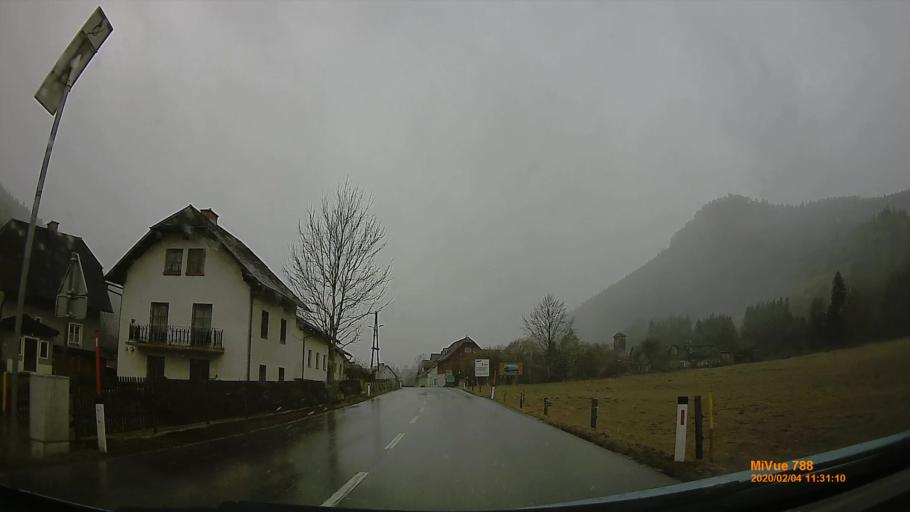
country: AT
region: Styria
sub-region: Politischer Bezirk Bruck-Muerzzuschlag
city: Neuberg an der Muerz
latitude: 47.6580
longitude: 15.5931
